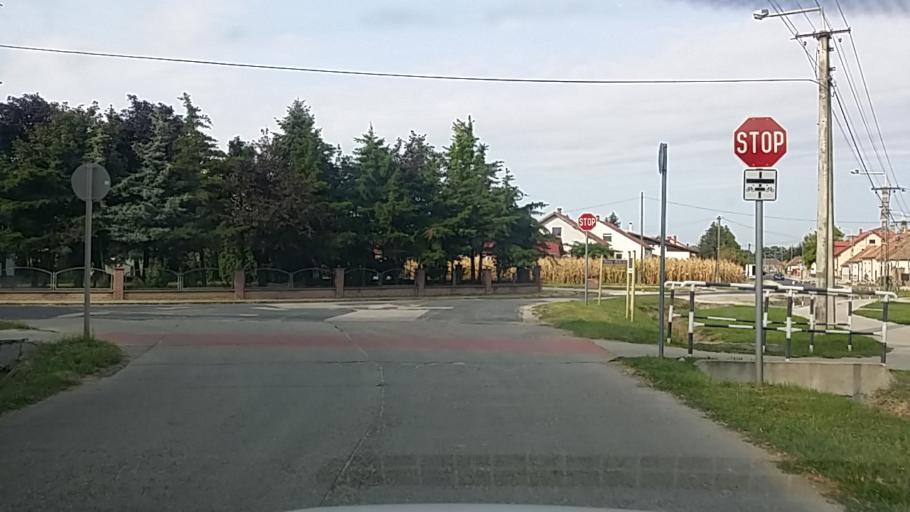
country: HU
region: Gyor-Moson-Sopron
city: Fertod
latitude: 47.6201
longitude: 16.8868
